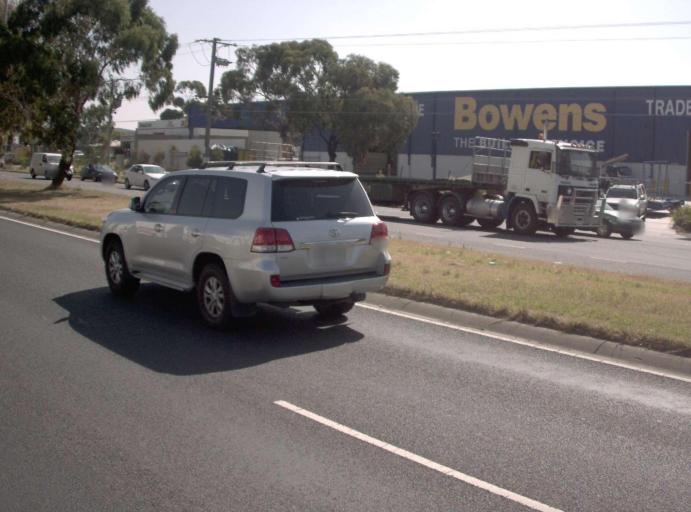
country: AU
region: Victoria
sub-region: Knox
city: Scoresby
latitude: -37.9102
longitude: 145.2364
